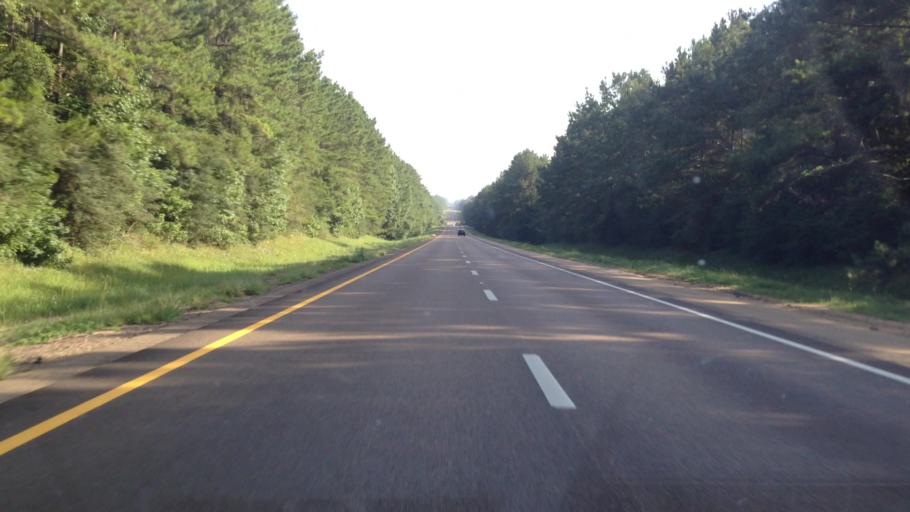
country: US
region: Mississippi
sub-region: Pike County
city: Summit
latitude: 31.3720
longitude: -90.4792
